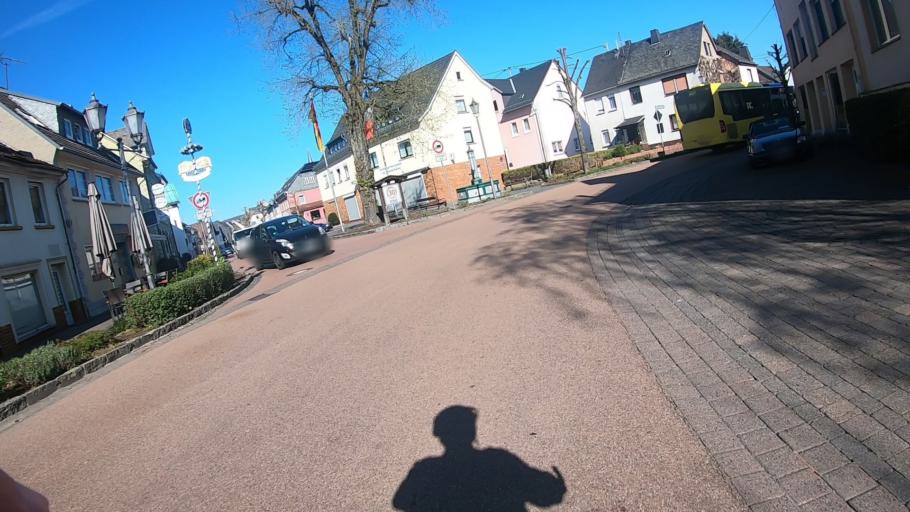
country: DE
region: Rheinland-Pfalz
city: Herschbach
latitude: 50.5725
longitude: 7.7354
